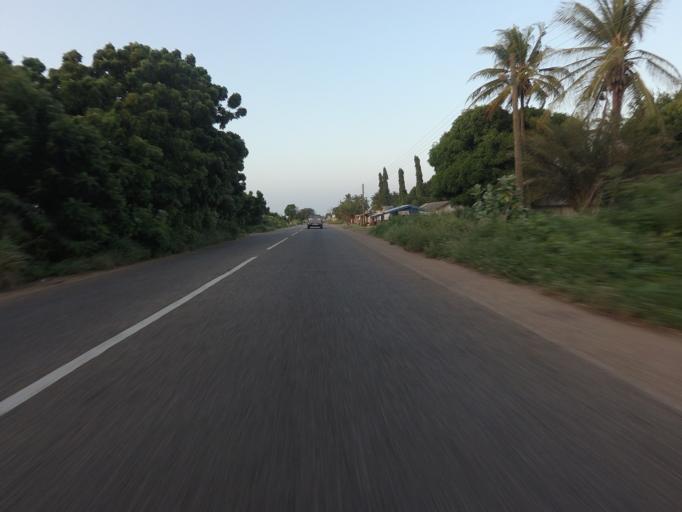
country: GH
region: Volta
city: Anloga
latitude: 5.8147
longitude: 0.9383
